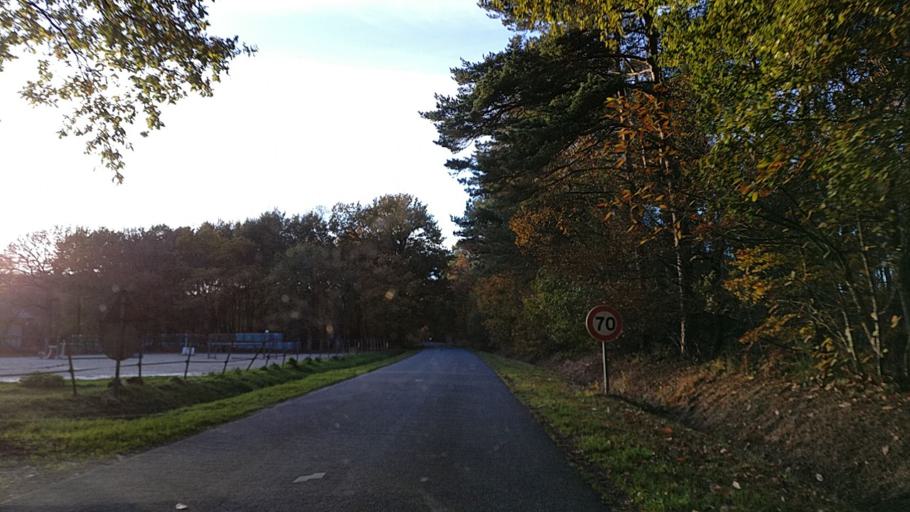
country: FR
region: Brittany
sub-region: Departement d'Ille-et-Vilaine
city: Liffre
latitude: 48.1895
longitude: -1.5269
